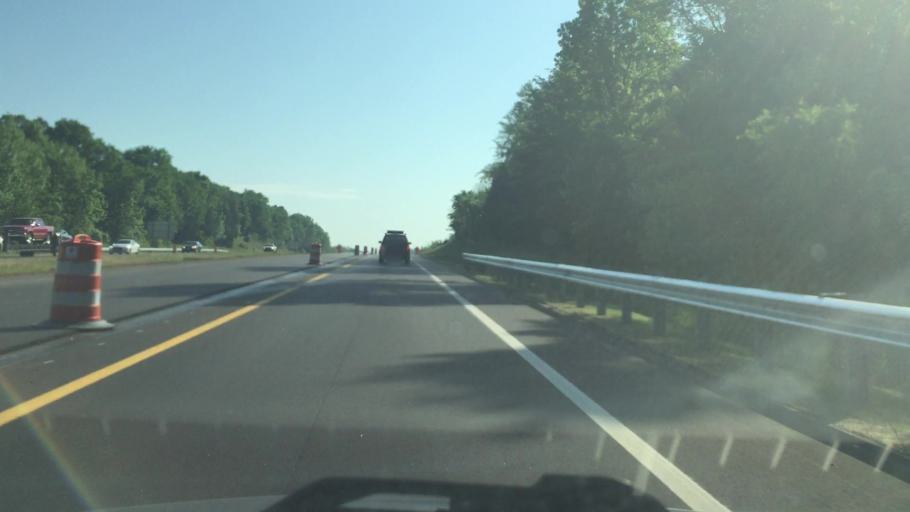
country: US
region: North Carolina
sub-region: Davie County
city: Mocksville
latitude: 35.9297
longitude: -80.5788
